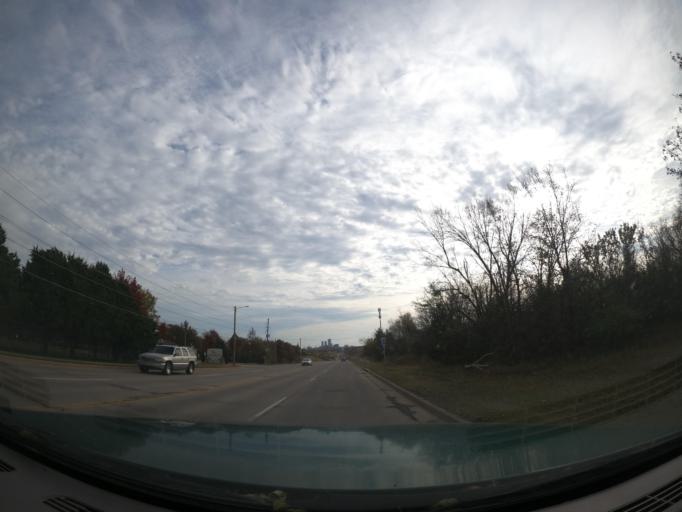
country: US
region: Oklahoma
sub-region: Tulsa County
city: Turley
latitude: 36.2091
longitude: -95.9936
